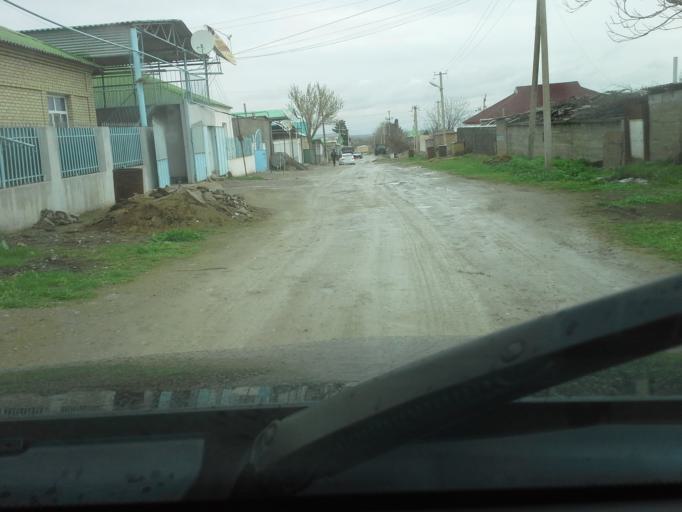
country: TM
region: Ahal
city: Abadan
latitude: 37.9643
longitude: 58.2098
